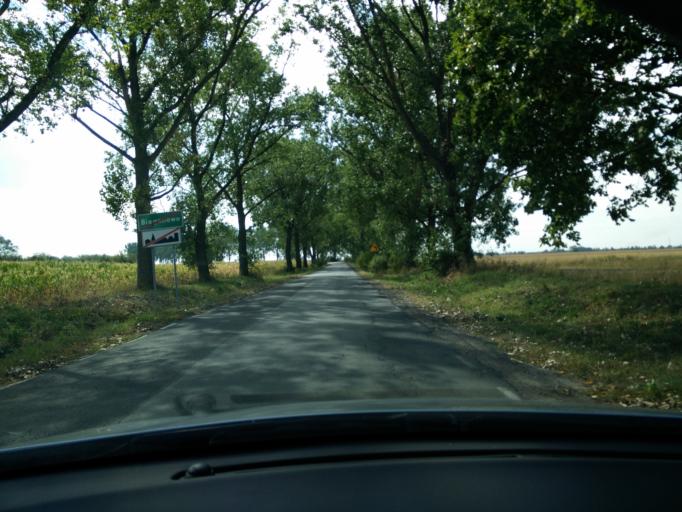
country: PL
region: Greater Poland Voivodeship
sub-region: Powiat poznanski
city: Kleszczewo
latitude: 52.2774
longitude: 17.2184
